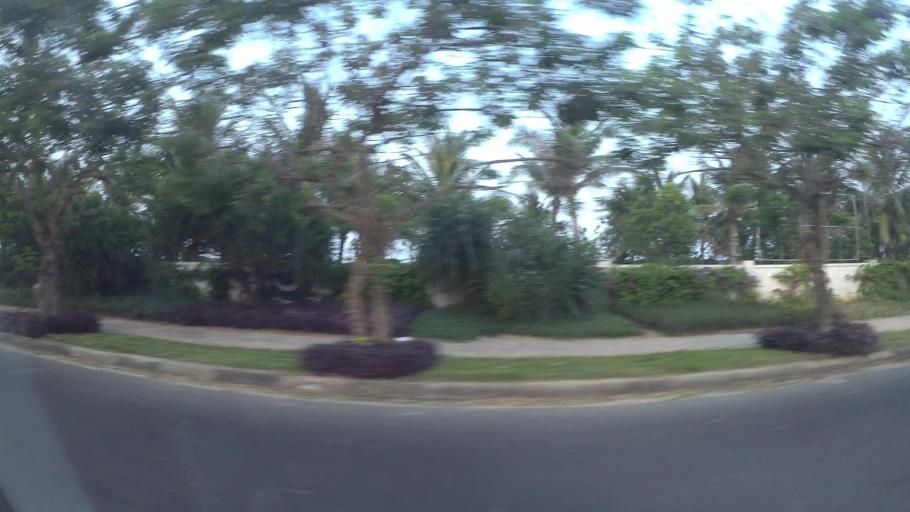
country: VN
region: Da Nang
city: Ngu Hanh Son
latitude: 16.0166
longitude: 108.2604
